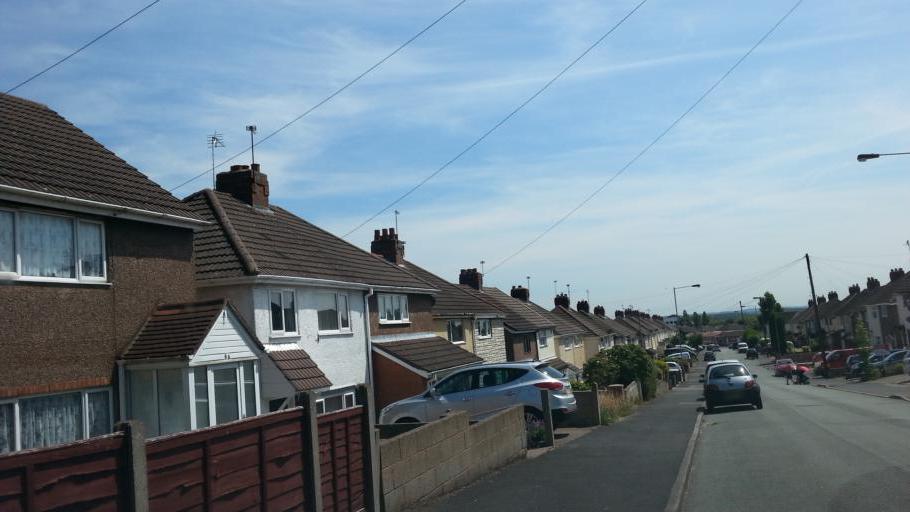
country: GB
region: England
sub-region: Staffordshire
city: Cannock
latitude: 52.7163
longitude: -2.0218
